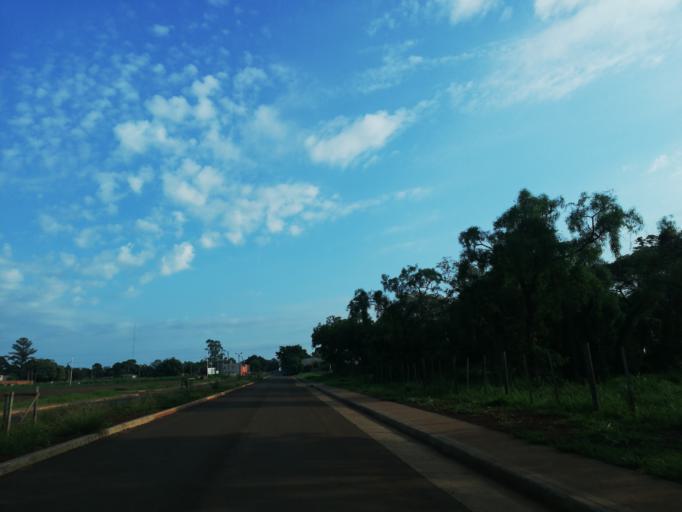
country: AR
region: Misiones
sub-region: Departamento de Capital
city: Posadas
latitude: -27.3933
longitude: -55.9239
